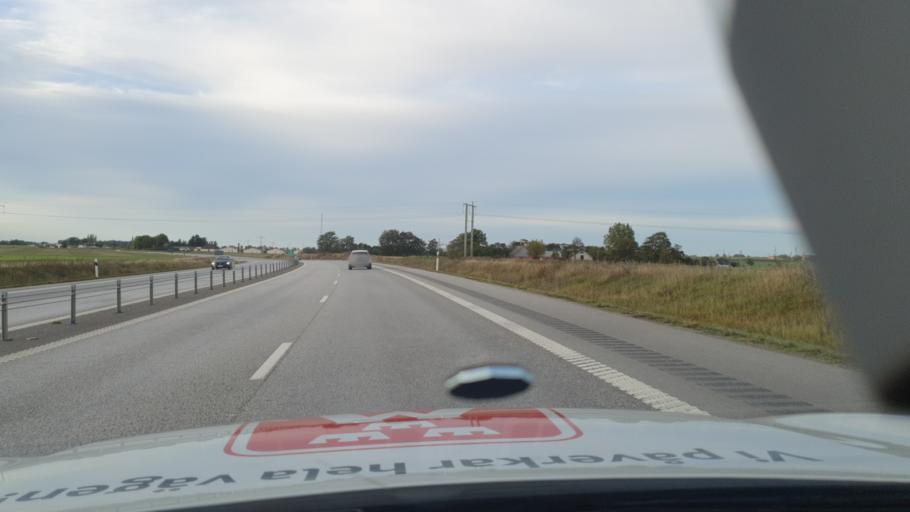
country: SE
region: Skane
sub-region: Trelleborgs Kommun
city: Skare
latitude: 55.4175
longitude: 13.0632
